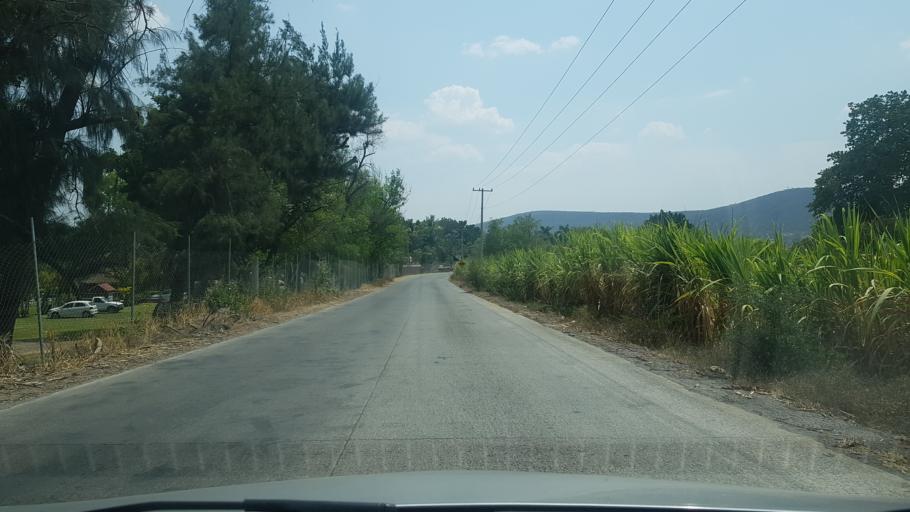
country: MX
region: Morelos
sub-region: Tlaltizapan de Zapata
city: Colonia Palo Prieto (Chipitongo)
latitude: 18.7357
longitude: -99.1147
